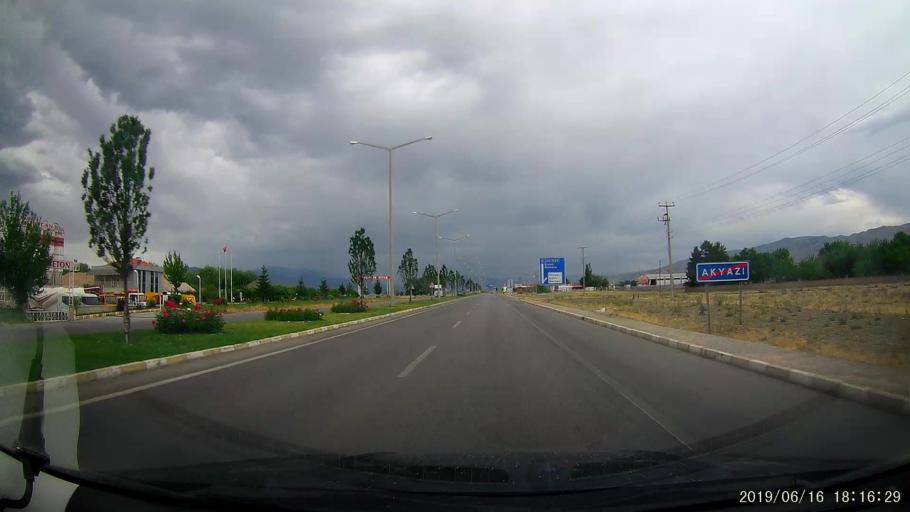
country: TR
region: Erzincan
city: Erzincan
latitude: 39.7286
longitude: 39.5475
